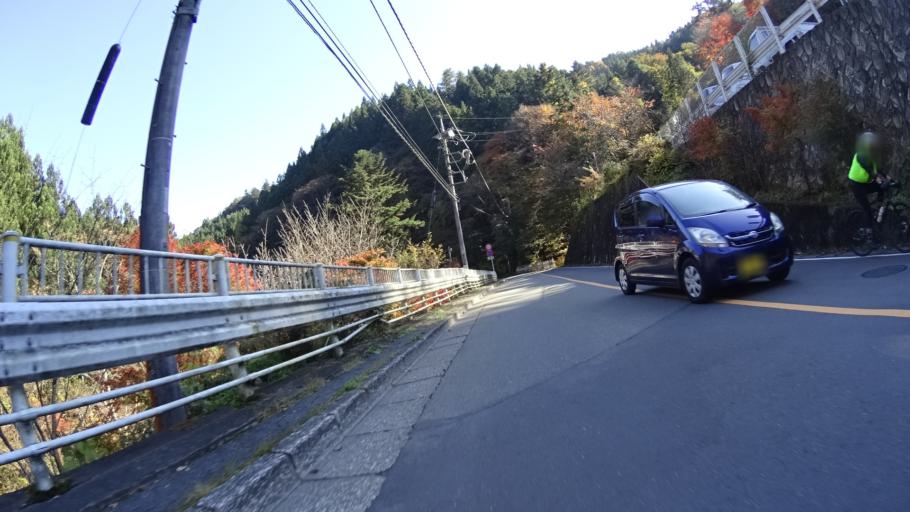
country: JP
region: Yamanashi
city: Uenohara
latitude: 35.7244
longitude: 139.0546
